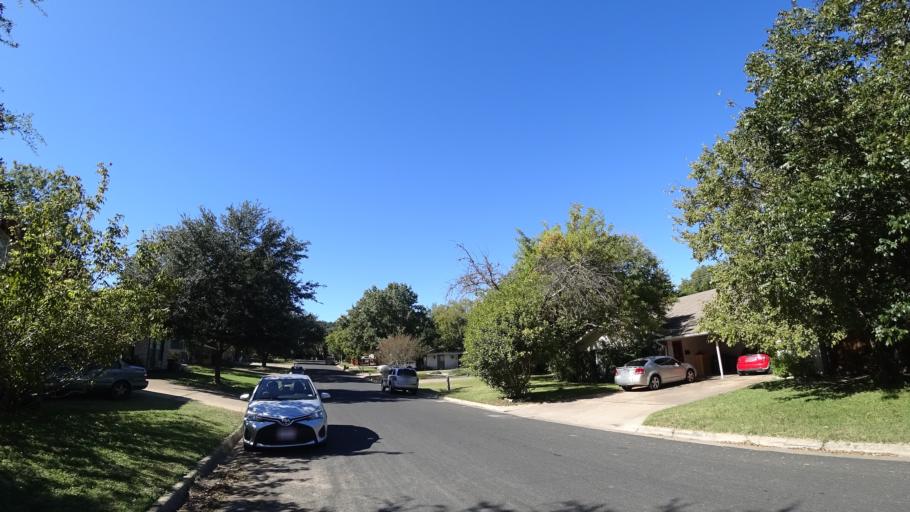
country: US
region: Texas
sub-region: Travis County
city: Rollingwood
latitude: 30.2368
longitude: -97.7770
